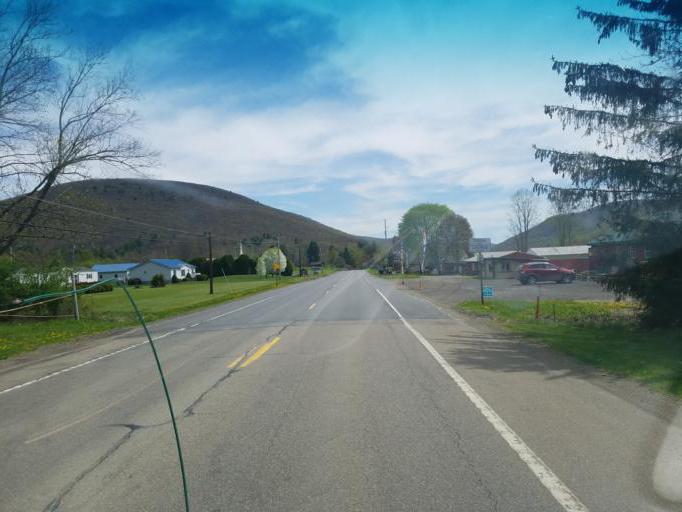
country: US
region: Pennsylvania
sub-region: Potter County
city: Galeton
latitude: 41.7445
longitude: -77.6042
